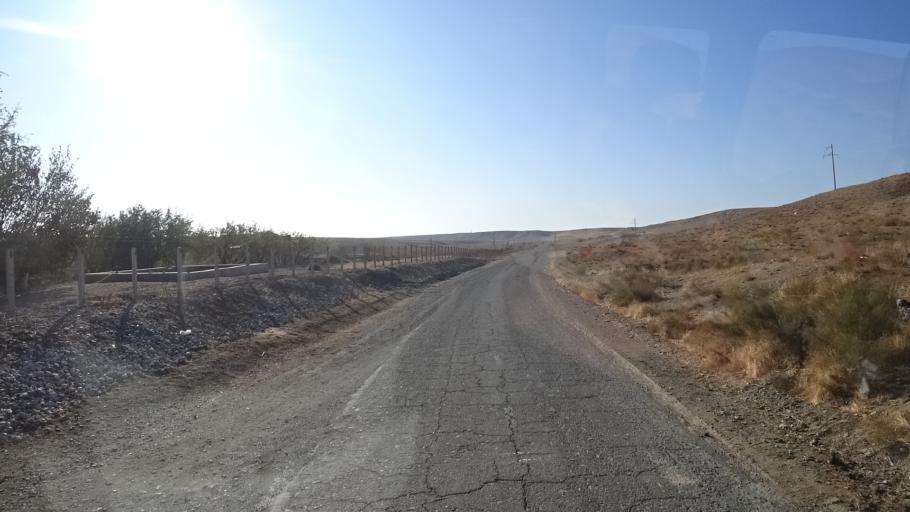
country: UZ
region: Navoiy
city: Beshrabot
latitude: 40.2578
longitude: 65.4557
